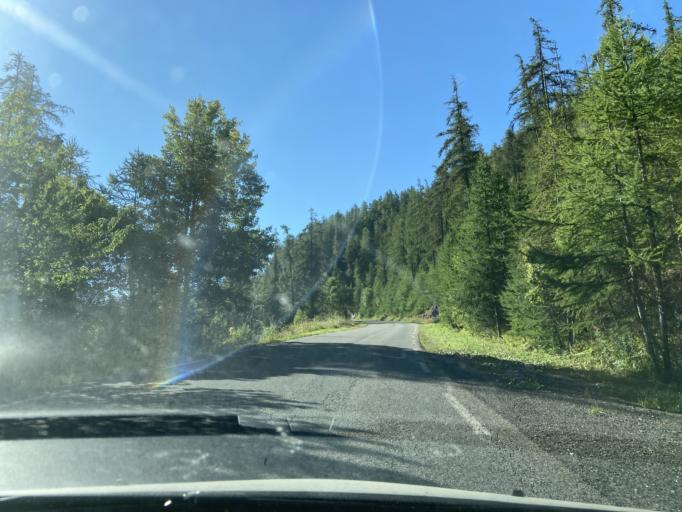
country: FR
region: Provence-Alpes-Cote d'Azur
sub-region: Departement des Hautes-Alpes
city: Guillestre
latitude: 44.6350
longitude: 6.6253
